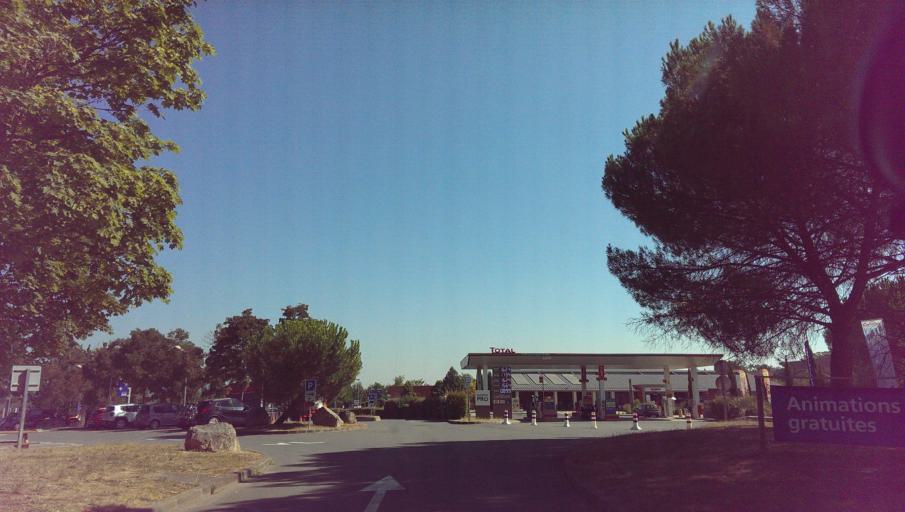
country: FR
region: Aquitaine
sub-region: Departement du Lot-et-Garonne
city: Sainte-Colombe-en-Bruilhois
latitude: 44.1991
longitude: 0.5076
